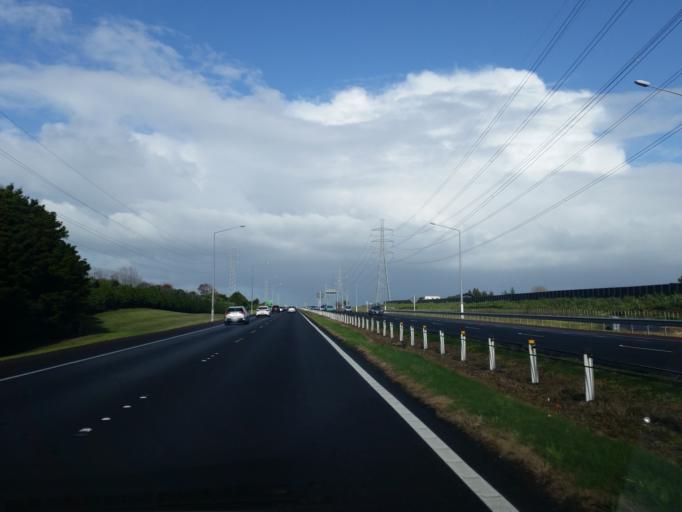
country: NZ
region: Auckland
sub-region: Auckland
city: Papakura
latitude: -37.0638
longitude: 174.9252
